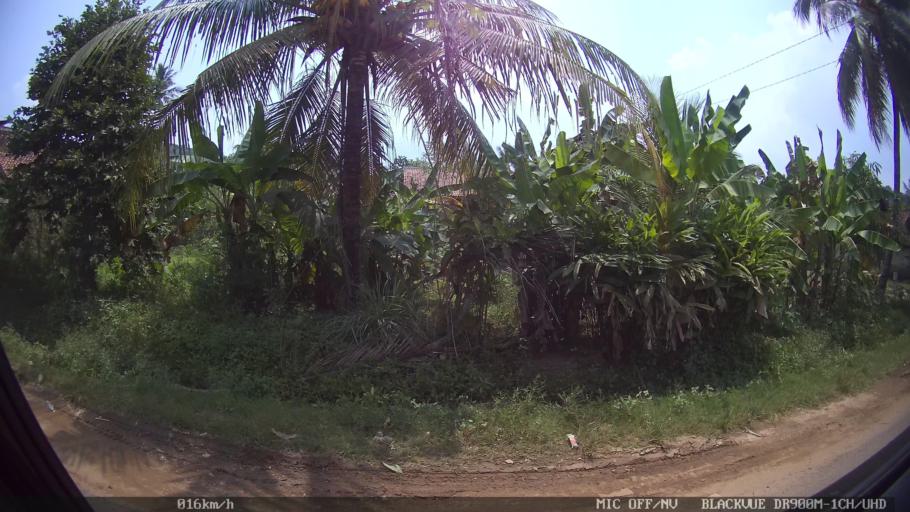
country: ID
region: Lampung
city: Pringsewu
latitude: -5.3807
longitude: 105.0002
